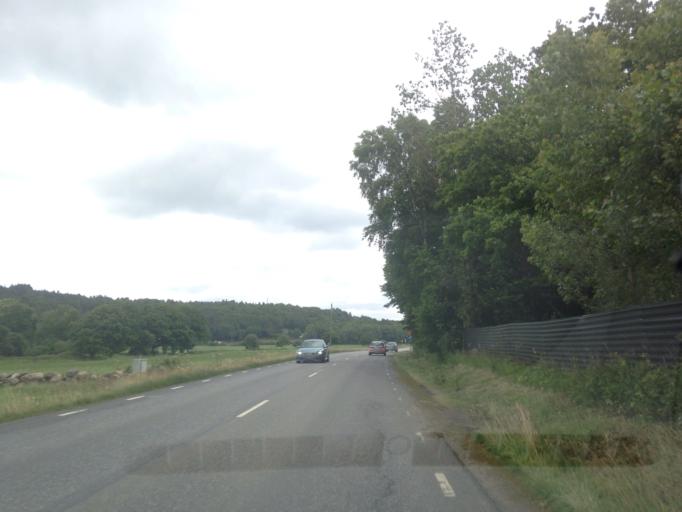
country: SE
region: Vaestra Goetaland
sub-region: Kungalvs Kommun
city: Kode
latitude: 57.8571
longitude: 11.8422
